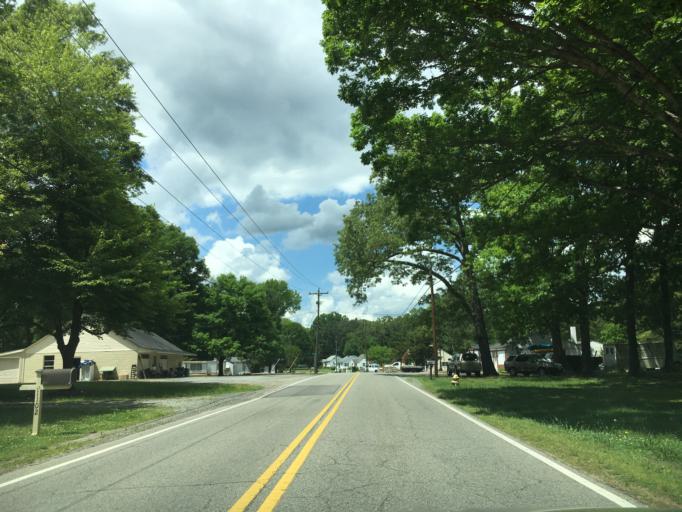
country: US
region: Virginia
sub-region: Halifax County
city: South Boston
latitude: 36.7033
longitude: -78.9254
